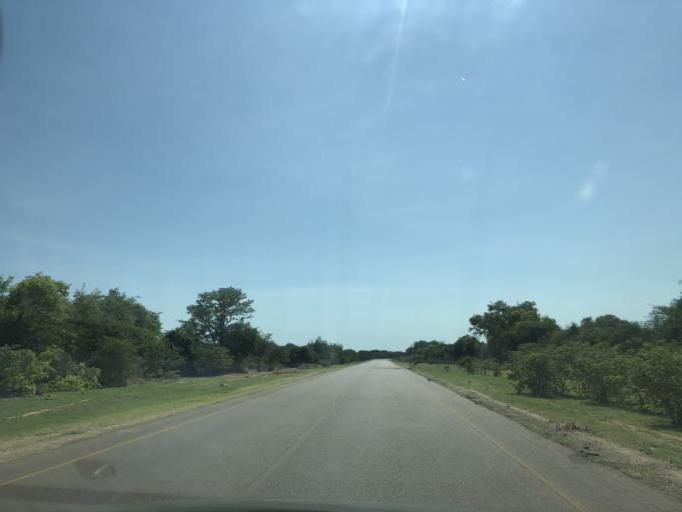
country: AO
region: Cunene
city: Ondjiva
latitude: -16.7109
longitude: 15.3036
